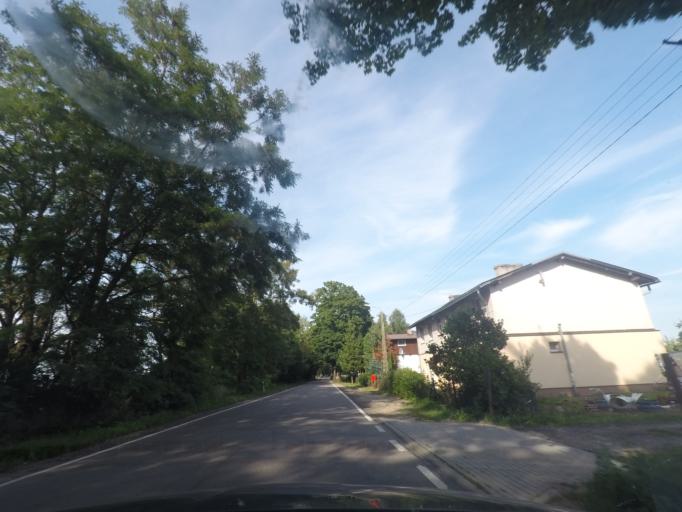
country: PL
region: Pomeranian Voivodeship
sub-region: Powiat leborski
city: Leba
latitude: 54.6411
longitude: 17.5361
